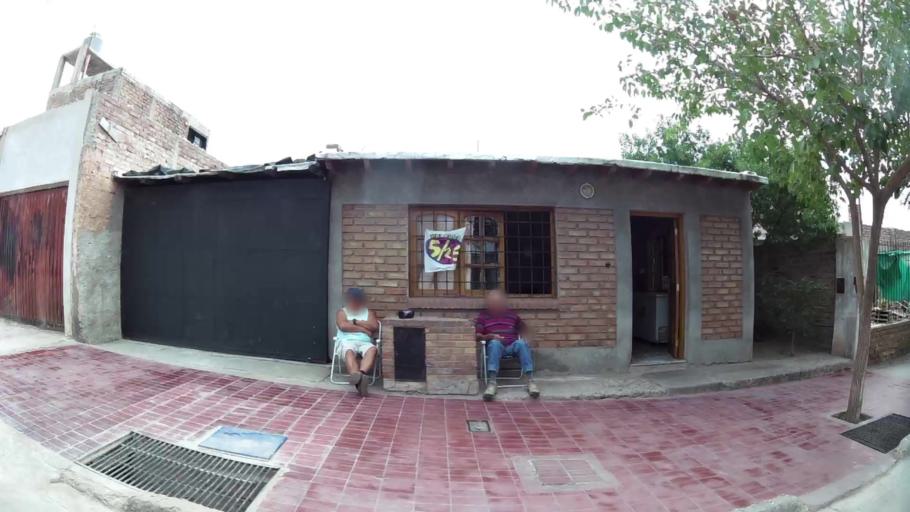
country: AR
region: Mendoza
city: Las Heras
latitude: -32.8580
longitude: -68.8684
